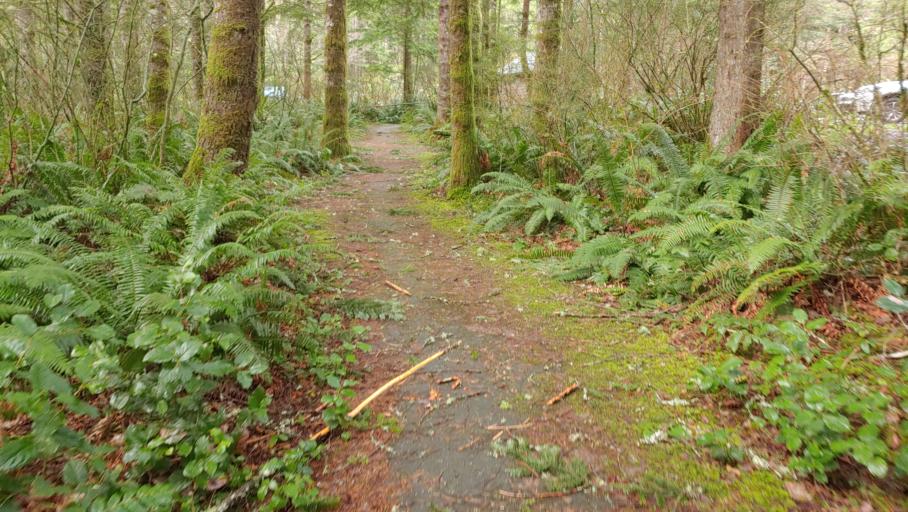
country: US
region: Washington
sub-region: King County
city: Hobart
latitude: 47.4678
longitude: -121.9358
